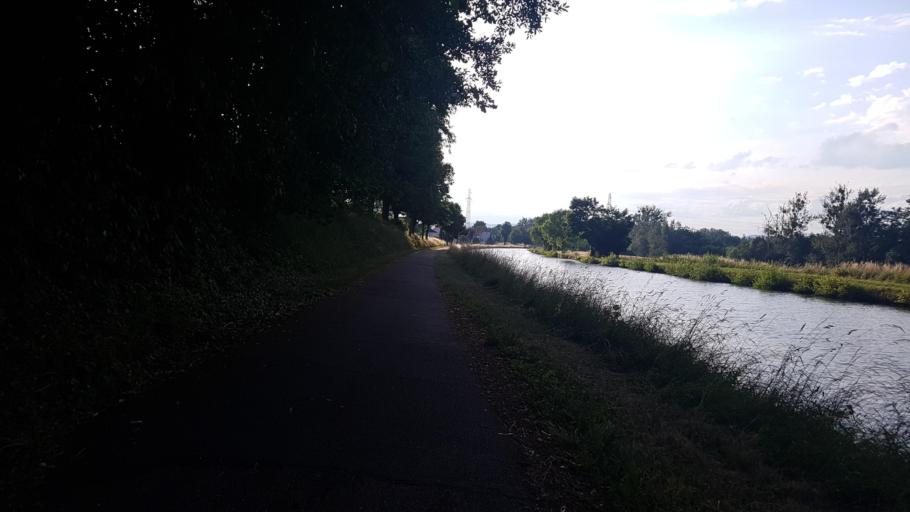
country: FR
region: Alsace
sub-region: Departement du Bas-Rhin
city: Dettwiller
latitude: 48.7448
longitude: 7.4706
